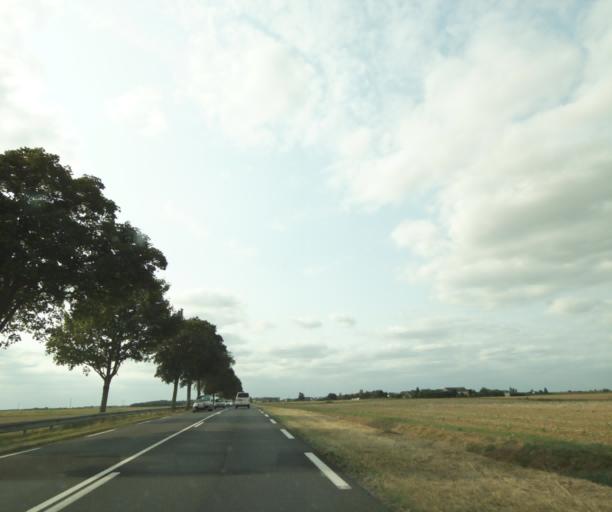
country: FR
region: Centre
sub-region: Departement d'Indre-et-Loire
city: Reignac-sur-Indre
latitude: 47.2320
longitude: 0.8737
